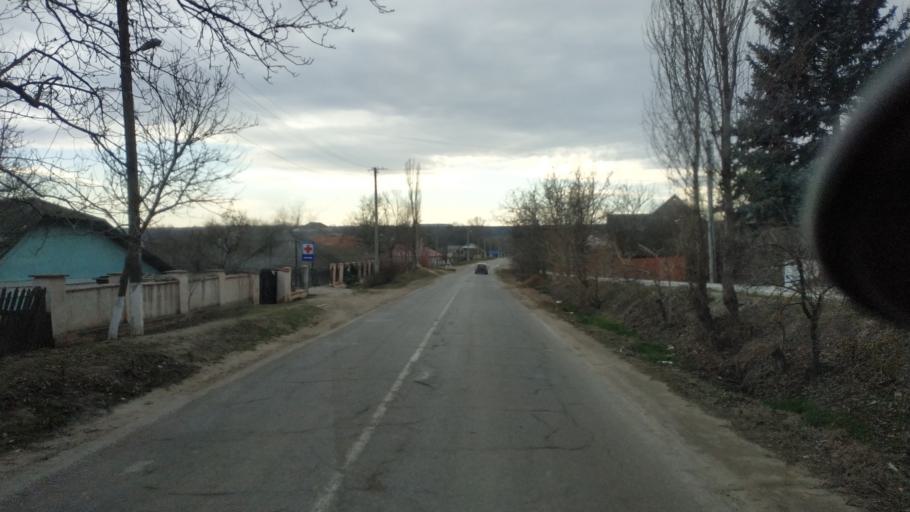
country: MD
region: Chisinau
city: Vadul lui Voda
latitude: 47.1443
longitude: 29.0706
